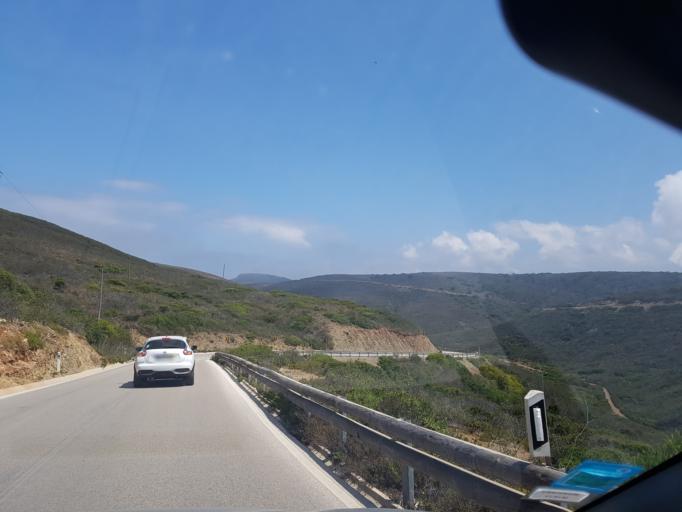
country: PT
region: Faro
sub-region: Vila do Bispo
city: Vila do Bispo
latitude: 37.1005
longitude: -8.9368
